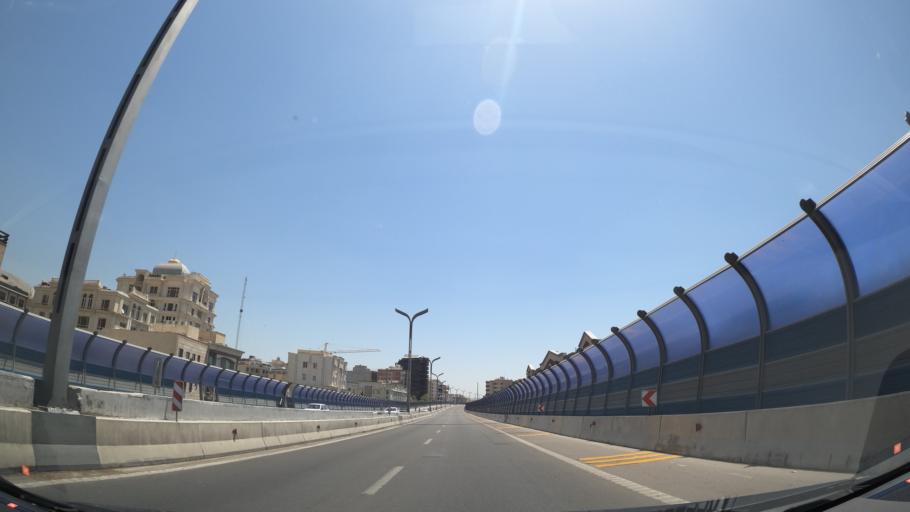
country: IR
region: Tehran
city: Tajrish
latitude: 35.7921
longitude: 51.4666
